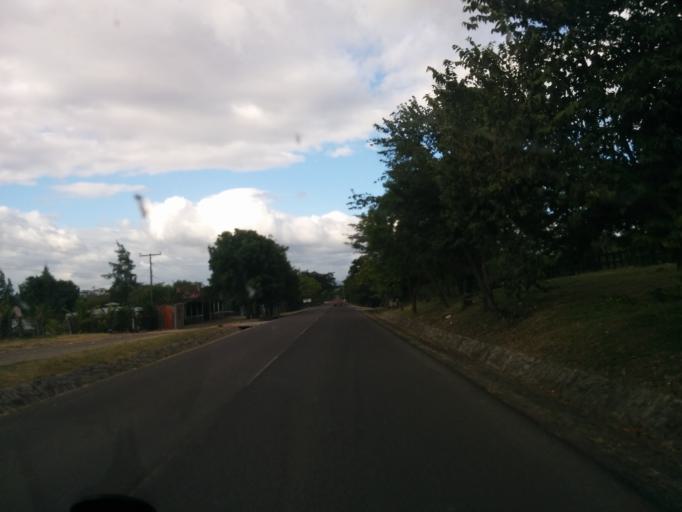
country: NI
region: Esteli
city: Esteli
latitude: 13.1587
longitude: -86.3696
